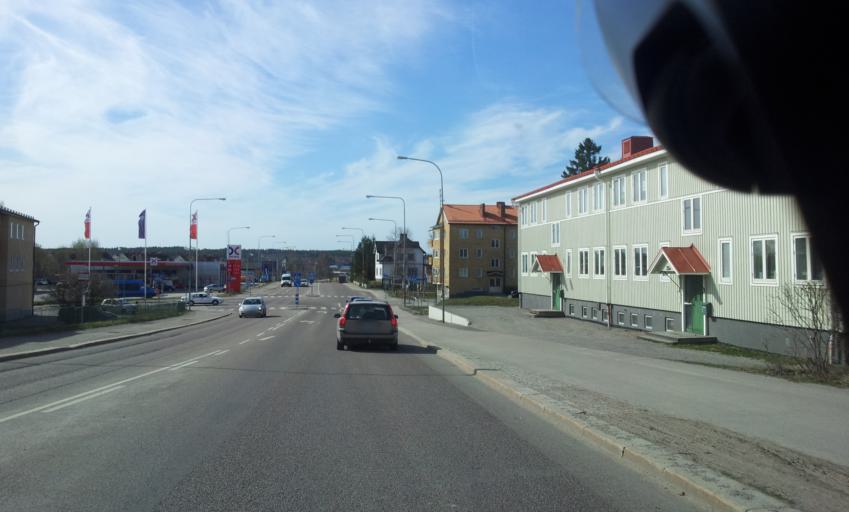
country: SE
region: Gaevleborg
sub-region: Hudiksvalls Kommun
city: Hudiksvall
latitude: 61.7203
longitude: 17.0985
